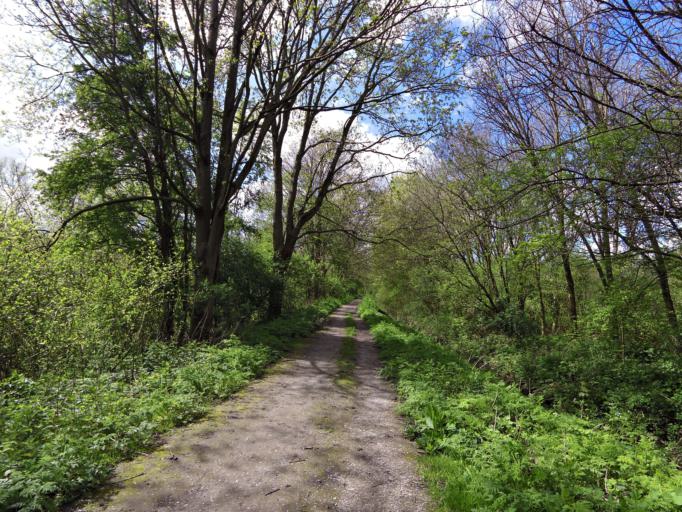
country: NL
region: South Holland
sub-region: Gemeente Binnenmaas
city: Heinenoord
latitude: 51.8376
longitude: 4.4497
